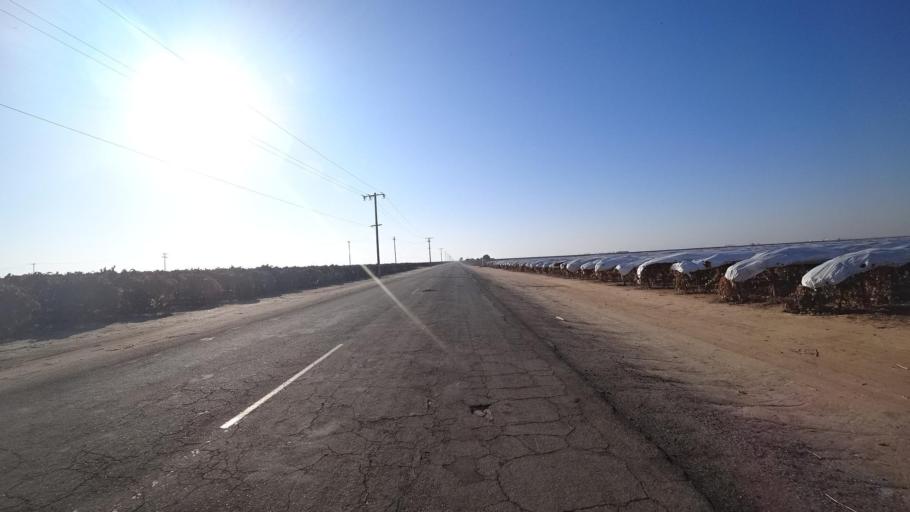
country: US
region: California
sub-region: Kern County
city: McFarland
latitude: 35.7338
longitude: -119.1695
